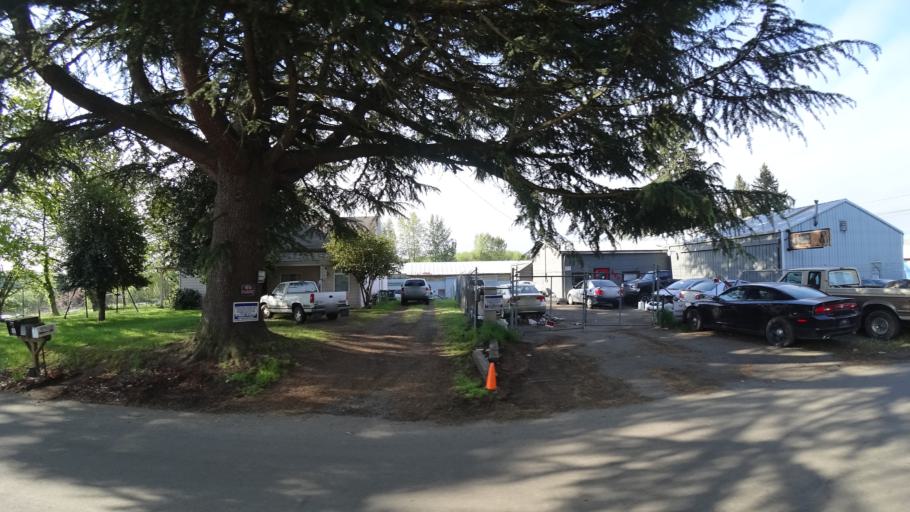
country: US
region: Oregon
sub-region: Washington County
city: Hillsboro
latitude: 45.5128
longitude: -122.9920
